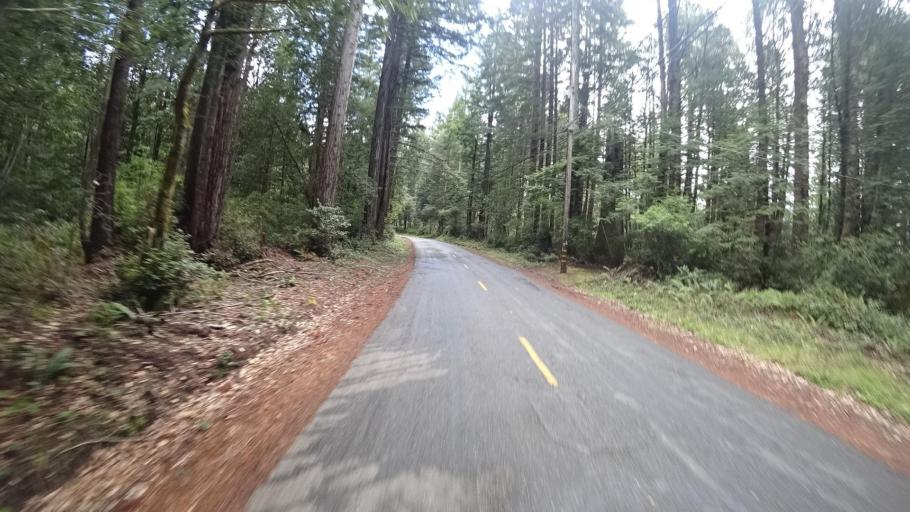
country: US
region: California
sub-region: Humboldt County
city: Bayside
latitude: 40.7778
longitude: -124.0070
